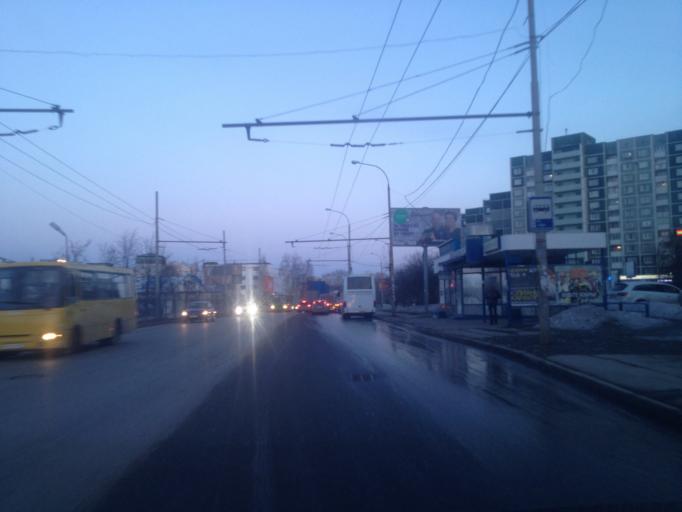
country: RU
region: Sverdlovsk
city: Yekaterinburg
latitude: 56.7945
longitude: 60.6343
